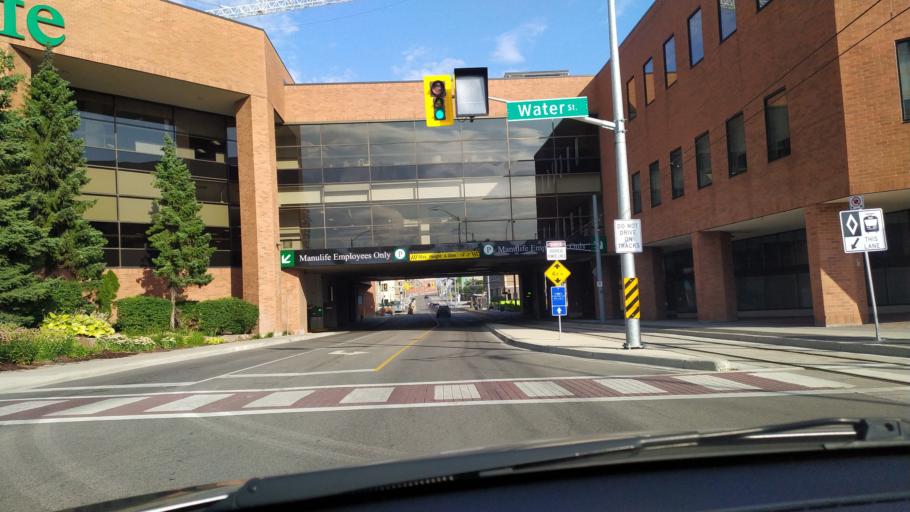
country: CA
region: Ontario
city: Waterloo
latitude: 43.4508
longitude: -80.4951
